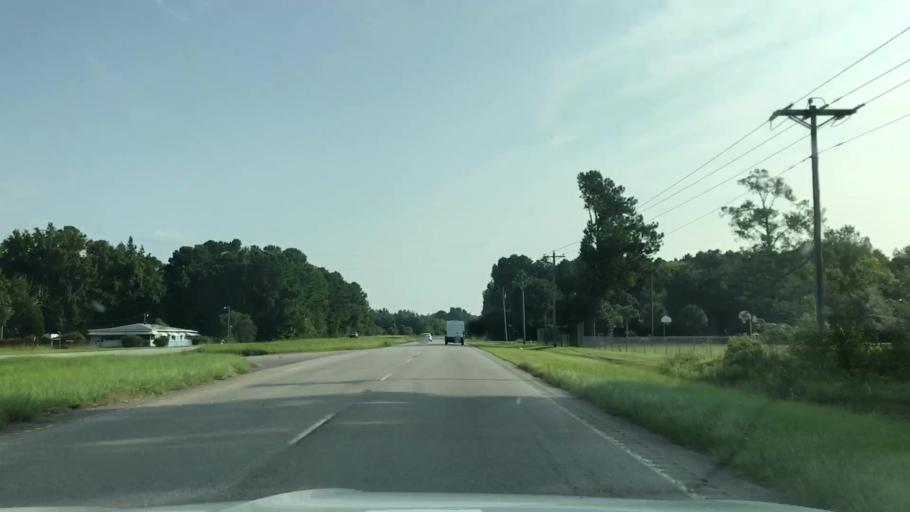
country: US
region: South Carolina
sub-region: Charleston County
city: Awendaw
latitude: 33.0238
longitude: -79.6302
